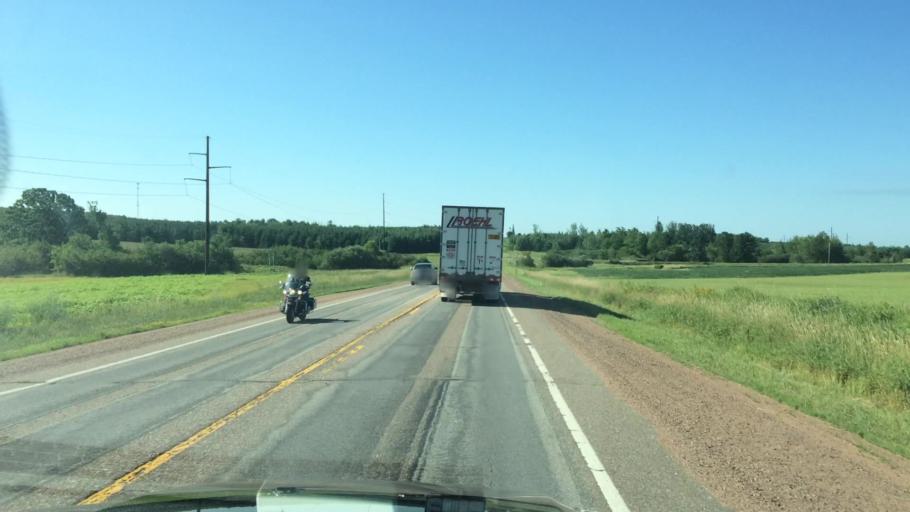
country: US
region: Wisconsin
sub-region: Marathon County
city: Athens
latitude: 44.9342
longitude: -90.0790
